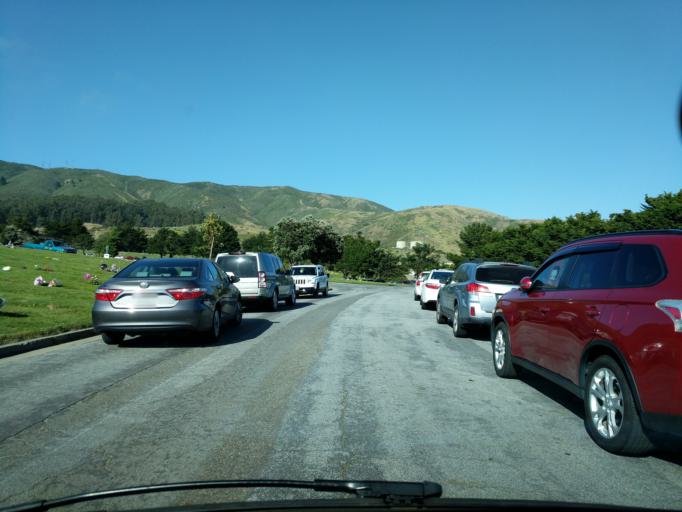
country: US
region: California
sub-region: San Mateo County
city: Colma
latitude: 37.6699
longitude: -122.4403
